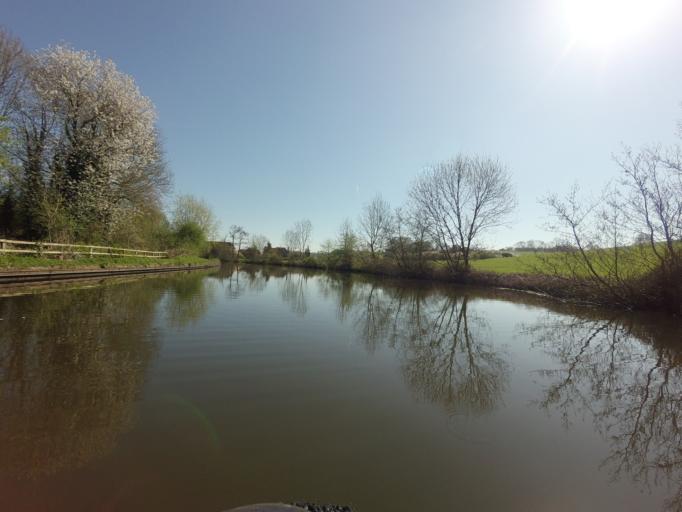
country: GB
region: England
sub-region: Hertfordshire
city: Rickmansworth
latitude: 51.6282
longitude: -0.4838
